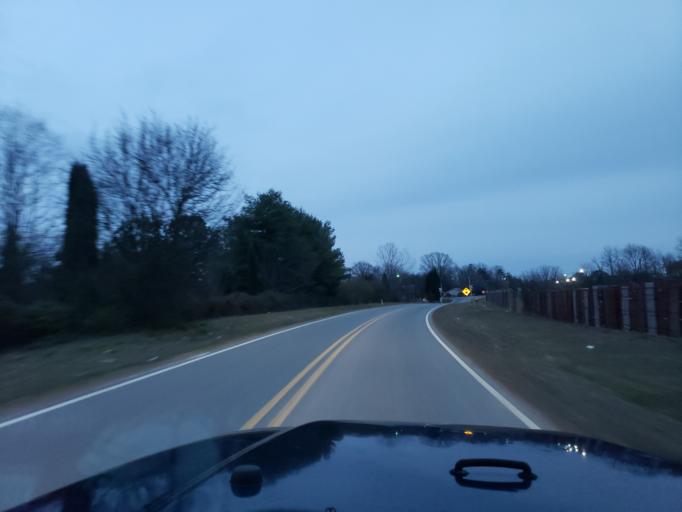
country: US
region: North Carolina
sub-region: Cleveland County
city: White Plains
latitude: 35.1838
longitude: -81.4201
